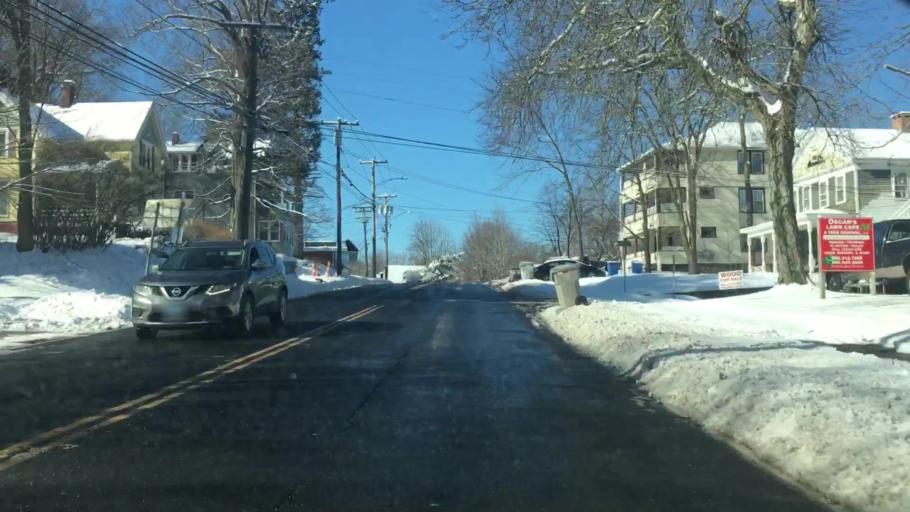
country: US
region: Connecticut
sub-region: Hartford County
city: Bristol
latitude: 41.6817
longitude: -72.9497
